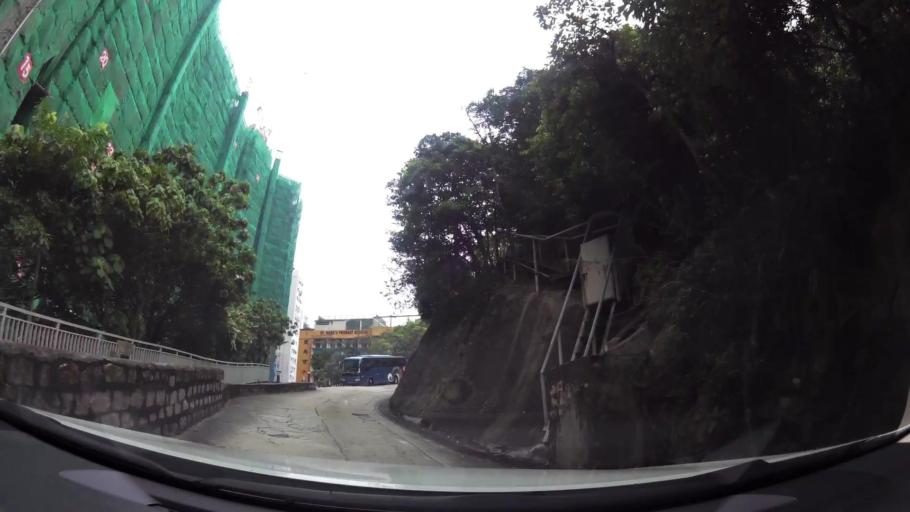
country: HK
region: Wanchai
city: Wan Chai
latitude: 22.2741
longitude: 114.2321
